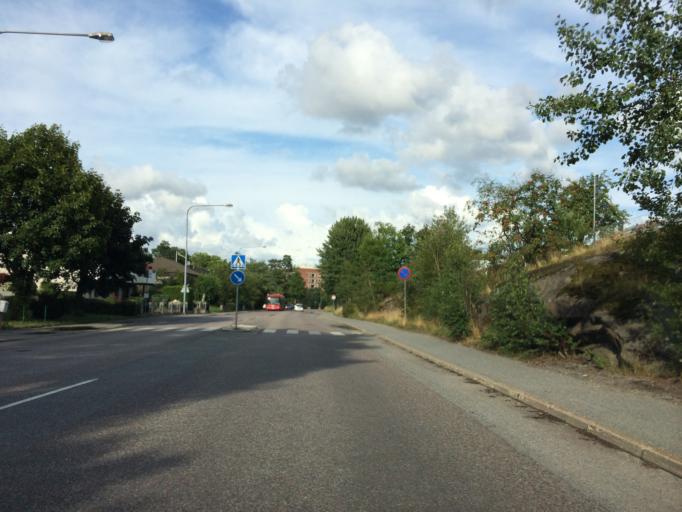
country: SE
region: Stockholm
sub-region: Huddinge Kommun
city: Segeltorp
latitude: 59.2810
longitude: 17.9536
